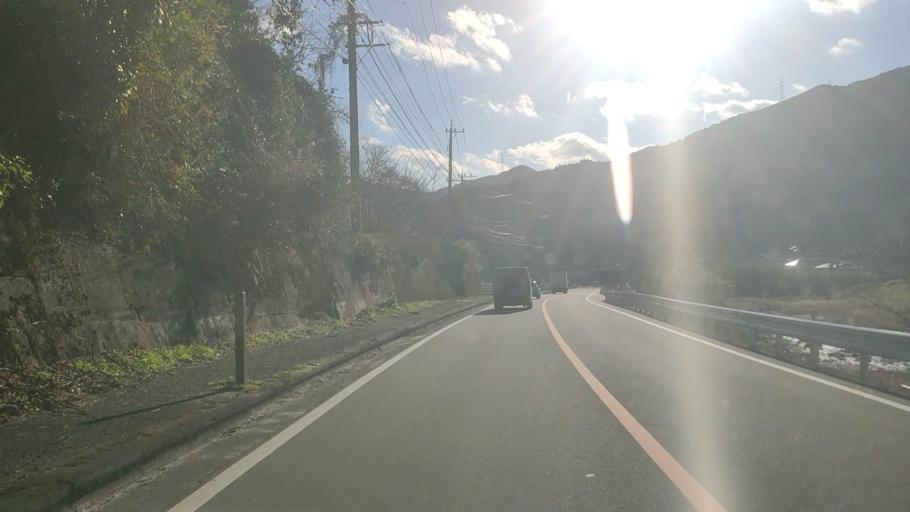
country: JP
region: Saga Prefecture
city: Saga-shi
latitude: 33.3560
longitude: 130.2512
